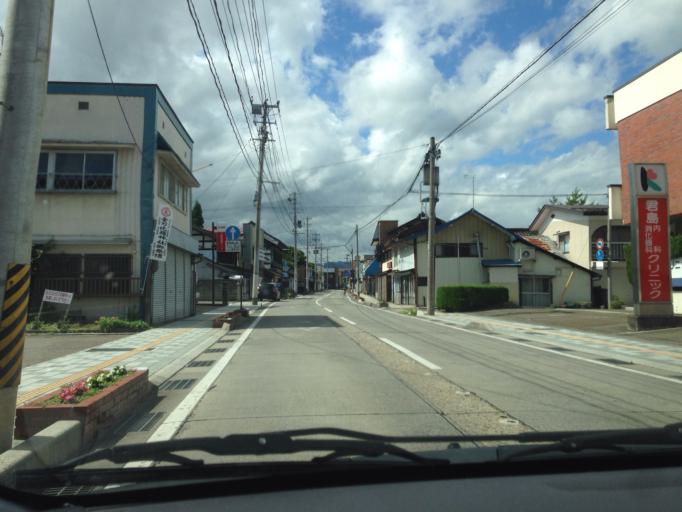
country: JP
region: Fukushima
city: Kitakata
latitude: 37.6556
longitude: 139.8726
